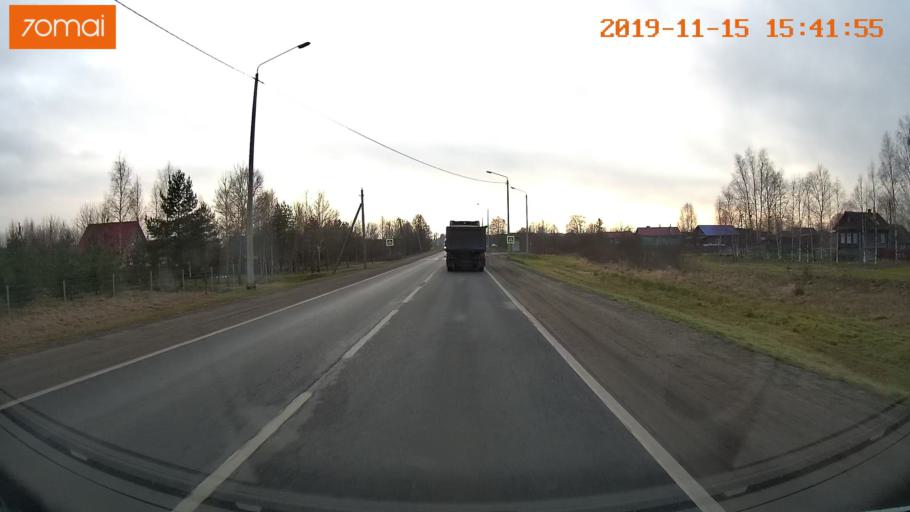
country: RU
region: Jaroslavl
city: Danilov
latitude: 57.9964
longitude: 40.0432
